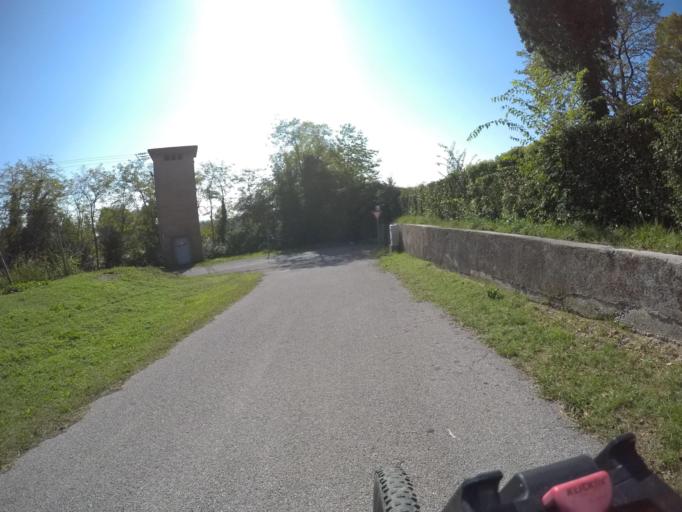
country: IT
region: Friuli Venezia Giulia
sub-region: Provincia di Udine
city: Manzano
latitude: 45.9924
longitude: 13.3863
